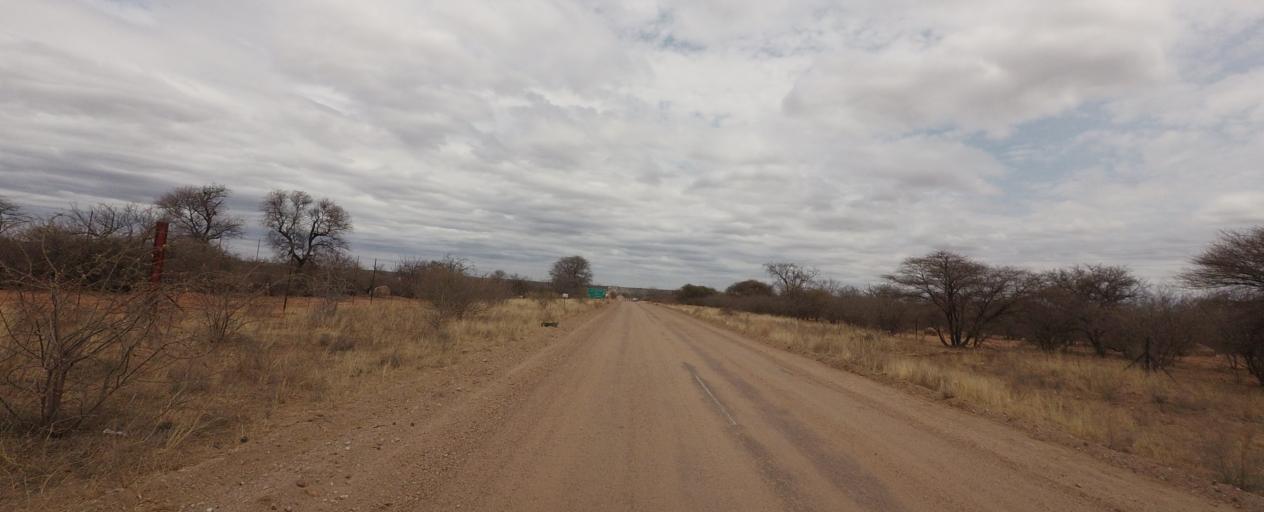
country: BW
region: Central
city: Mathathane
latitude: -22.6805
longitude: 28.6604
